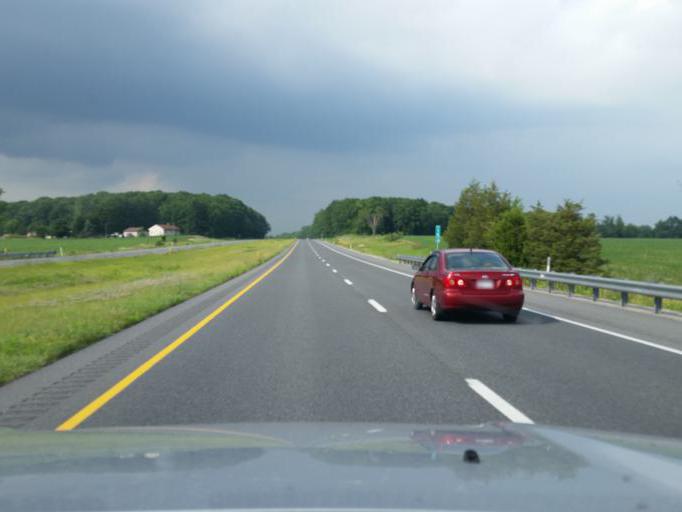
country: US
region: Pennsylvania
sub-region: Adams County
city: Biglerville
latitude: 39.8990
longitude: -77.1735
